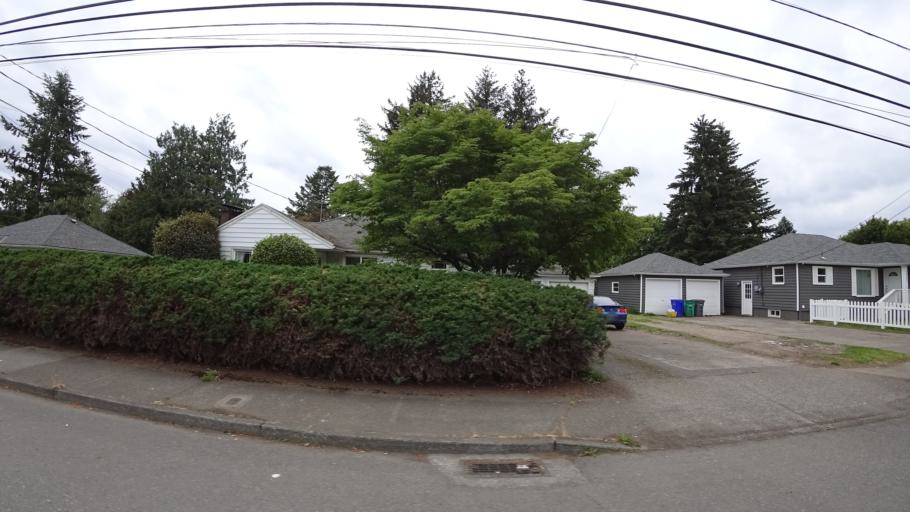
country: US
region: Oregon
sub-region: Multnomah County
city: Lents
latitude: 45.5091
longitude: -122.5481
